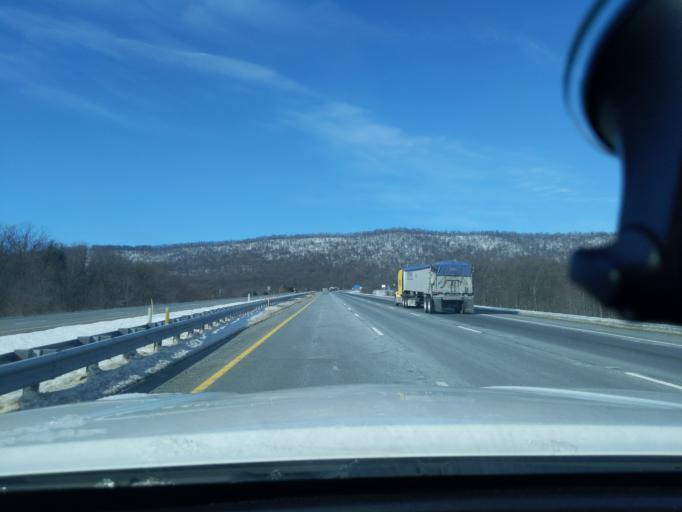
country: US
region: Maryland
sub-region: Washington County
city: Hancock
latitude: 39.7089
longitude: -78.2687
